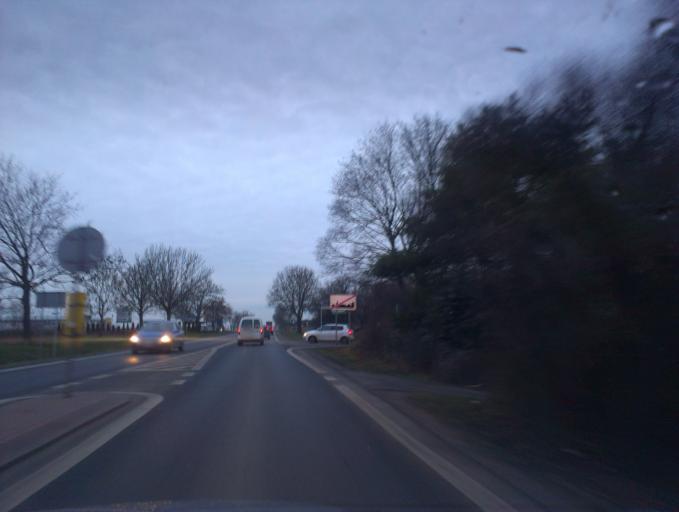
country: PL
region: Greater Poland Voivodeship
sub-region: Powiat poznanski
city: Suchy Las
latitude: 52.4789
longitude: 16.8681
